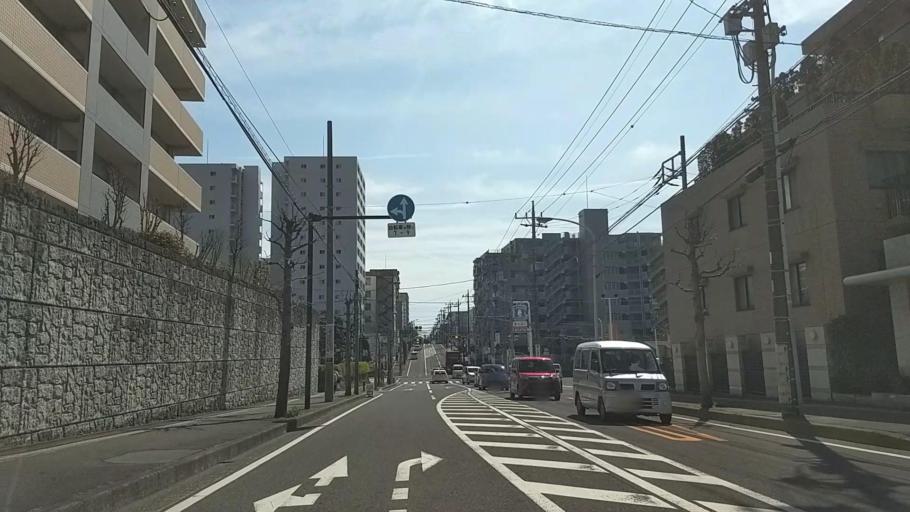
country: JP
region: Kanagawa
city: Fujisawa
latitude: 35.3979
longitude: 139.4626
